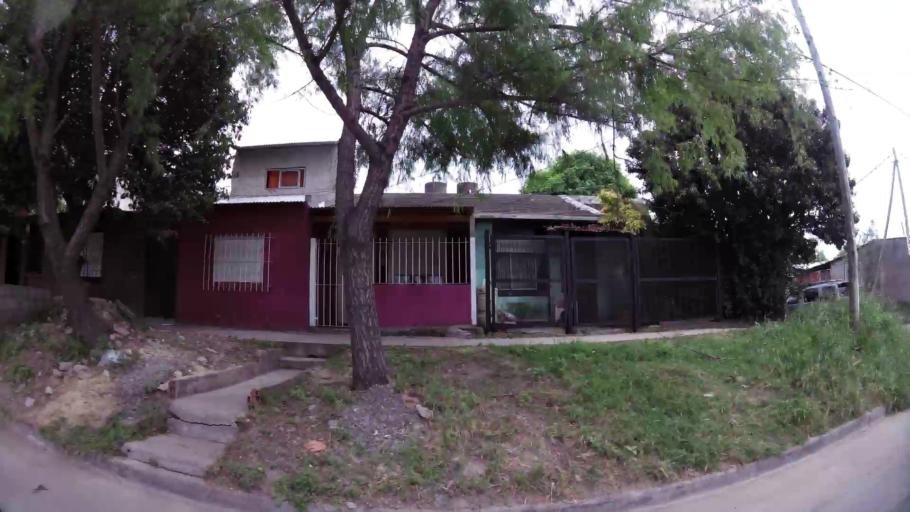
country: AR
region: Buenos Aires
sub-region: Partido de Avellaneda
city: Avellaneda
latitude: -34.6603
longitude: -58.3409
